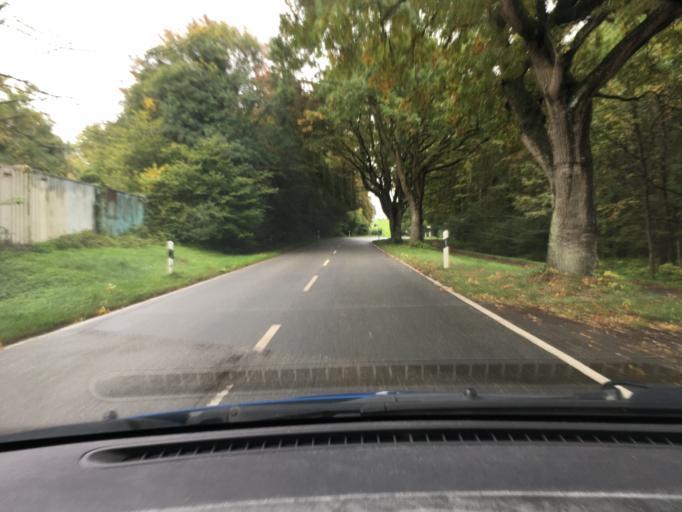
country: DE
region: Schleswig-Holstein
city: Bosdorf
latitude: 54.1380
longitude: 10.4817
